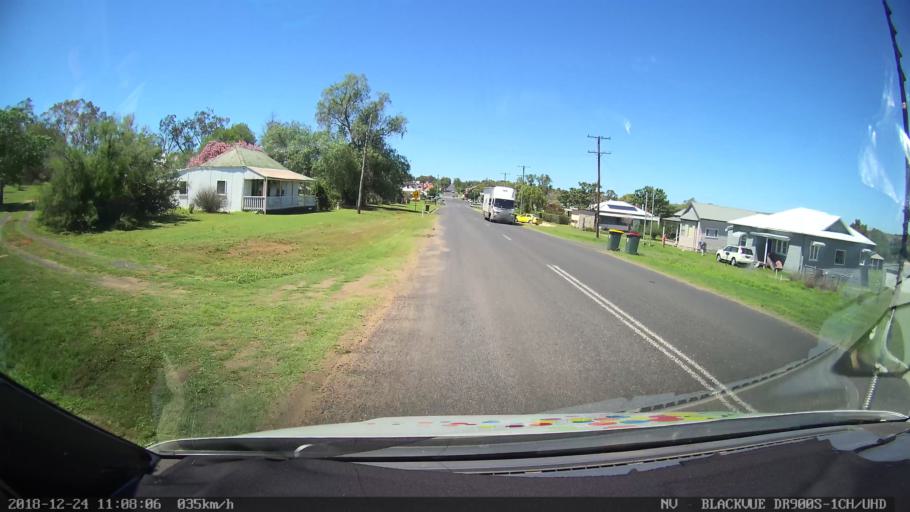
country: AU
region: New South Wales
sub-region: Upper Hunter Shire
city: Merriwa
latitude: -32.1357
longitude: 150.3565
